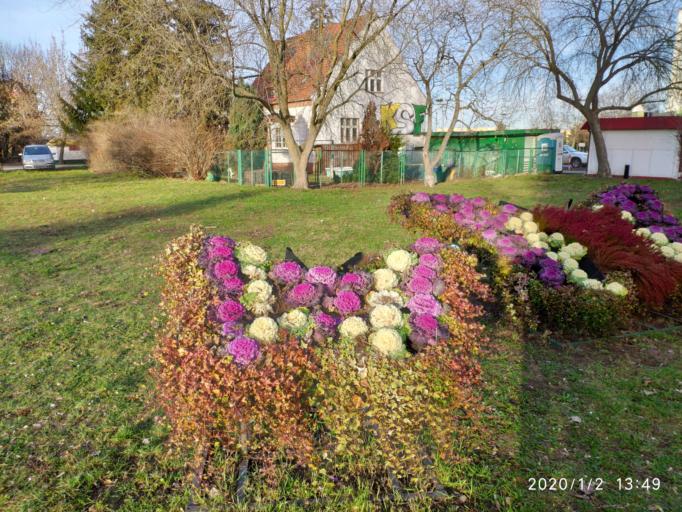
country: PL
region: Lubusz
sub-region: Zielona Gora
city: Zielona Gora
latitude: 51.9291
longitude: 15.4921
